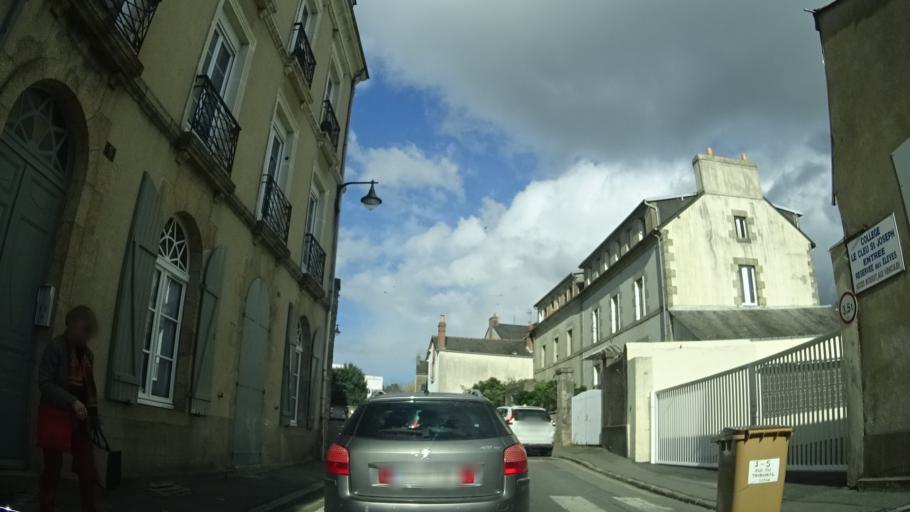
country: FR
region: Brittany
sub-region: Departement d'Ille-et-Vilaine
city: Redon
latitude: 47.6518
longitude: -2.0814
